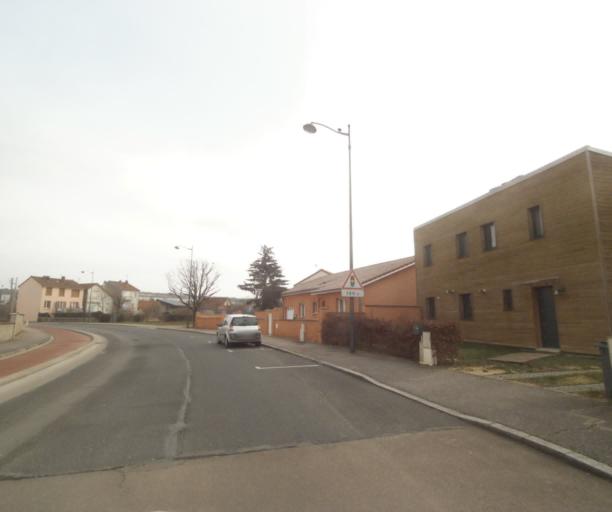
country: FR
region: Champagne-Ardenne
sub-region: Departement de la Haute-Marne
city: Bettancourt-la-Ferree
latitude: 48.6374
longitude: 4.9699
